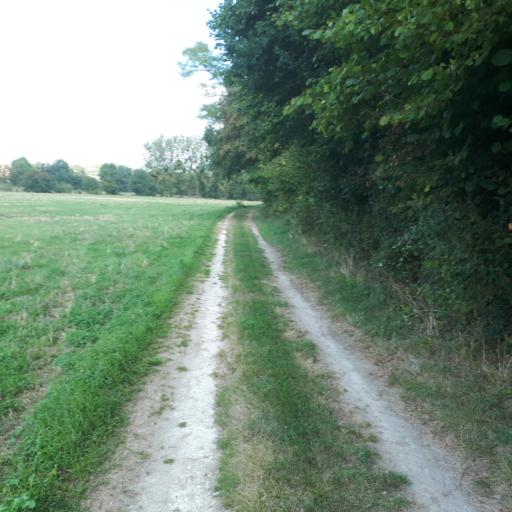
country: FR
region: Centre
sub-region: Departement du Loir-et-Cher
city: Villiers-sur-Loir
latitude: 47.8155
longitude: 0.9612
